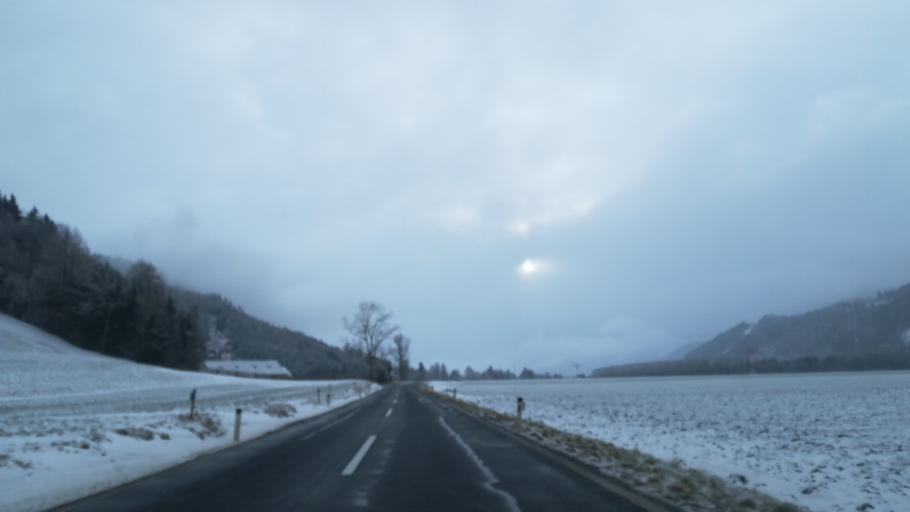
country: AT
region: Styria
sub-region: Politischer Bezirk Murtal
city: Poels
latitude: 47.2133
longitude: 14.6205
